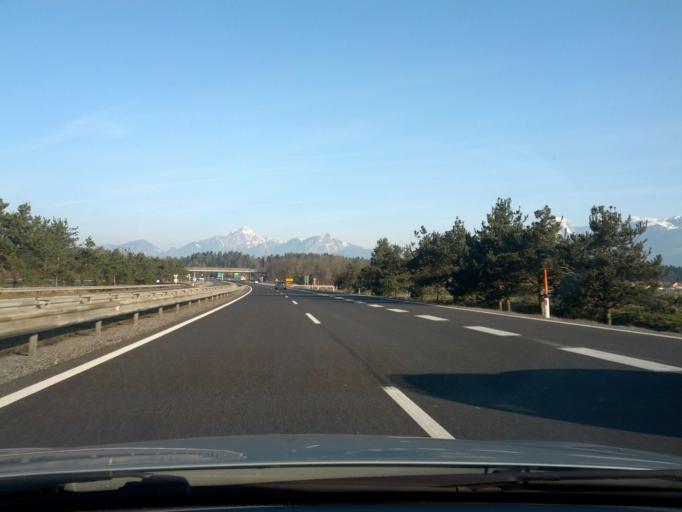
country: SI
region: Vodice
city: Vodice
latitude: 46.1804
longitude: 14.4852
